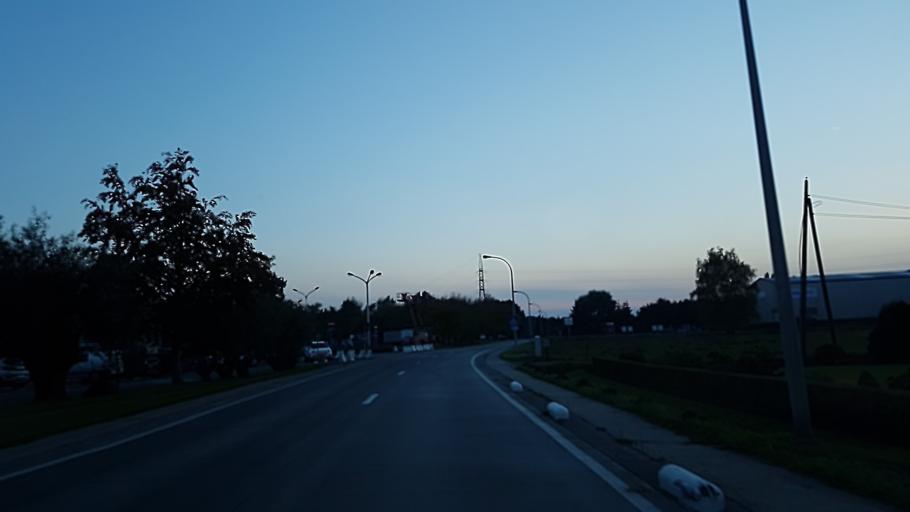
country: BE
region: Flanders
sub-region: Provincie Antwerpen
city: Duffel
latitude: 51.0852
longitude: 4.4786
